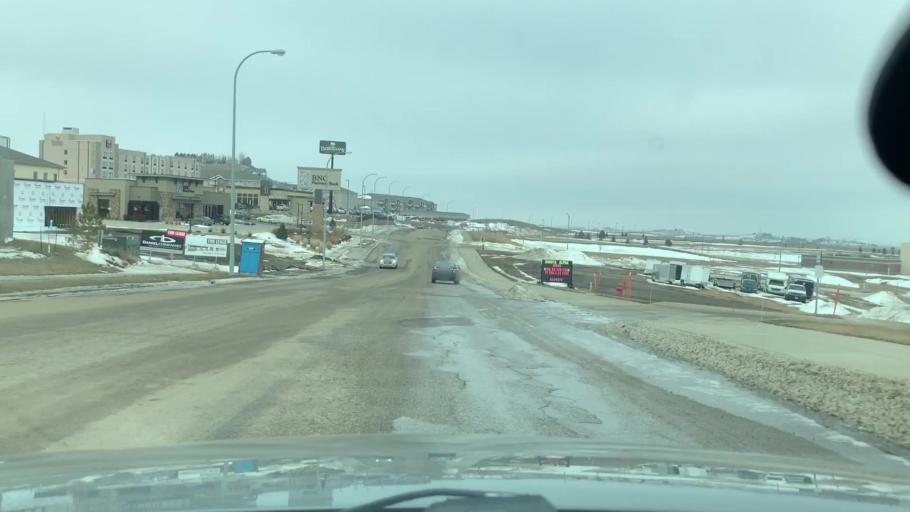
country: US
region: North Dakota
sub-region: Morton County
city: Mandan
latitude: 46.8489
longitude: -100.9089
